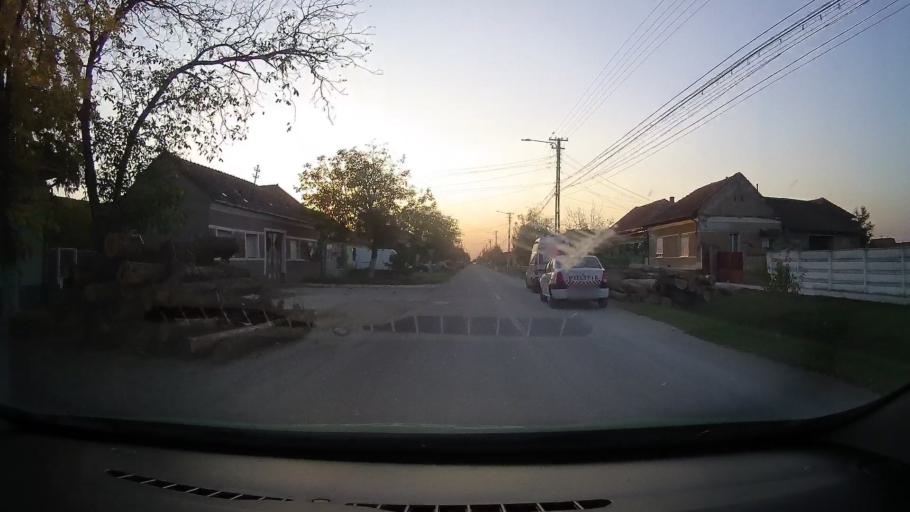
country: RO
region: Arad
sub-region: Comuna Seleus
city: Seleus
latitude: 46.3841
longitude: 21.7061
